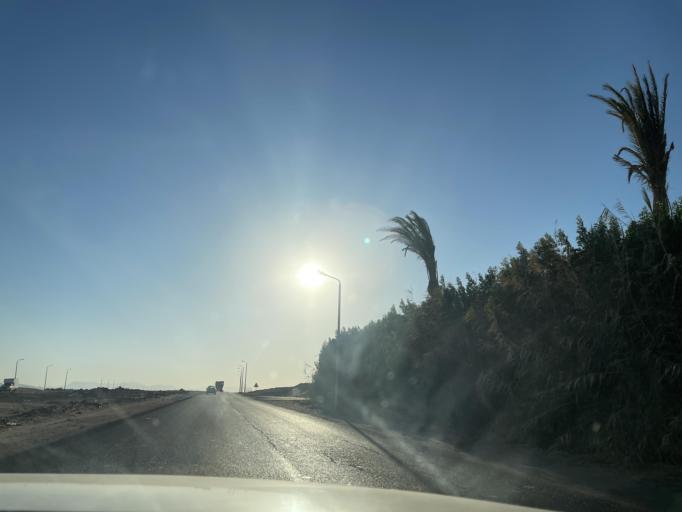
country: EG
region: Red Sea
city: Hurghada
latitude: 27.2180
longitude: 33.7944
